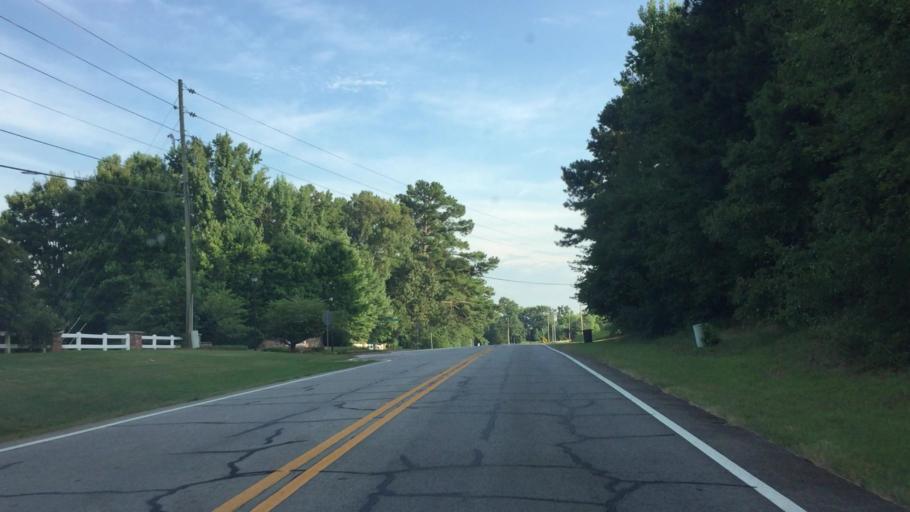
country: US
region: Georgia
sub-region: Henry County
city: Stockbridge
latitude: 33.5749
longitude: -84.1473
